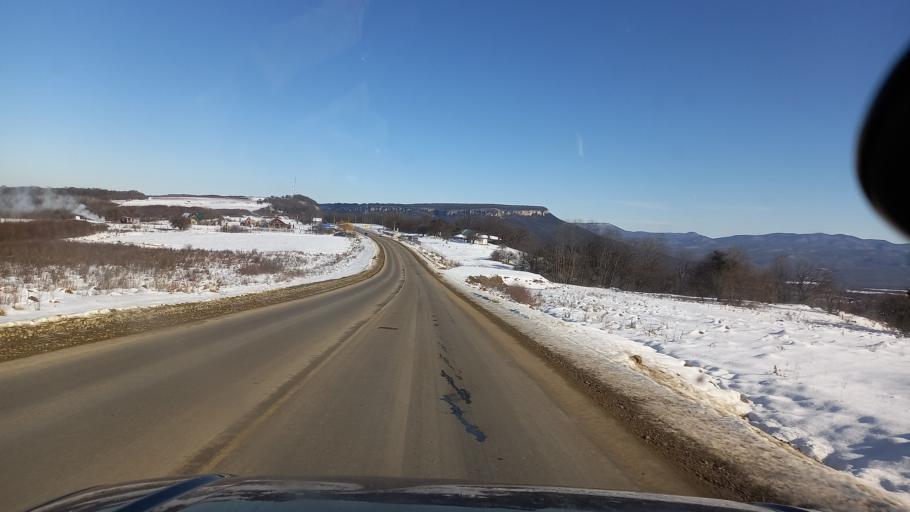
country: RU
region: Adygeya
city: Kamennomostskiy
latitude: 44.2325
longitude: 40.1432
